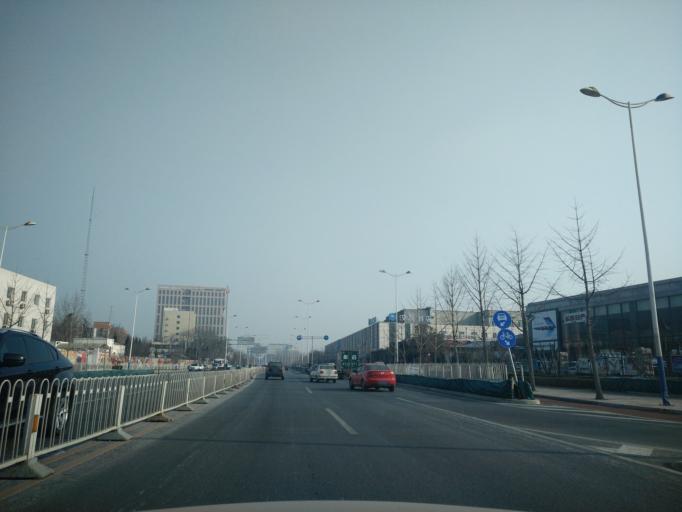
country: CN
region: Beijing
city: Daxing
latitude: 39.7422
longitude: 116.3171
